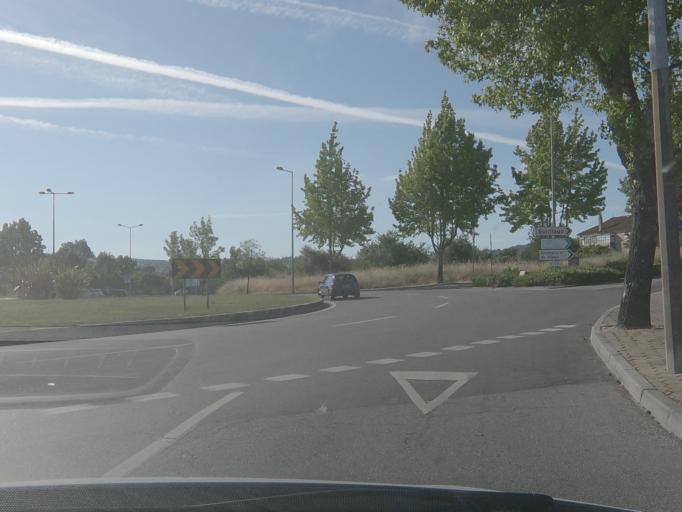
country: PT
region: Viseu
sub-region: Viseu
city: Viseu
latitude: 40.6682
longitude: -7.9018
